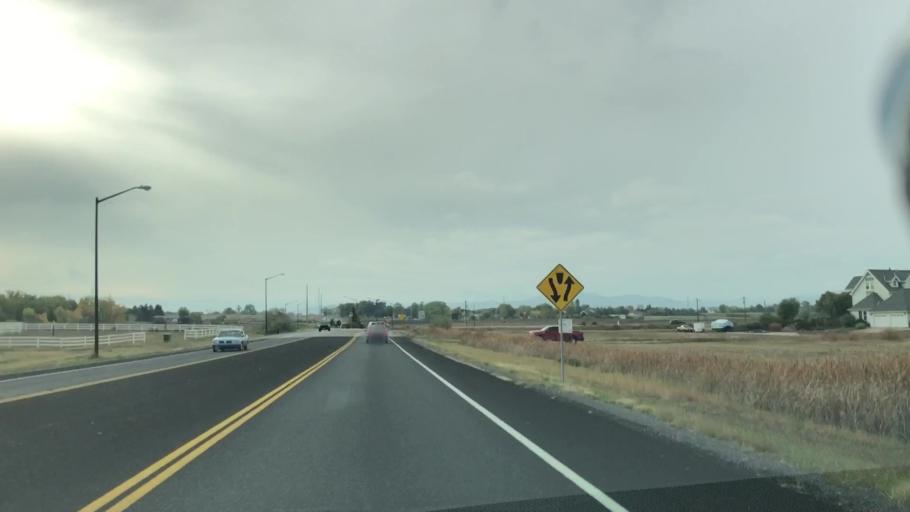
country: US
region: Colorado
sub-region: Larimer County
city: Loveland
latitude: 40.4657
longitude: -105.0365
